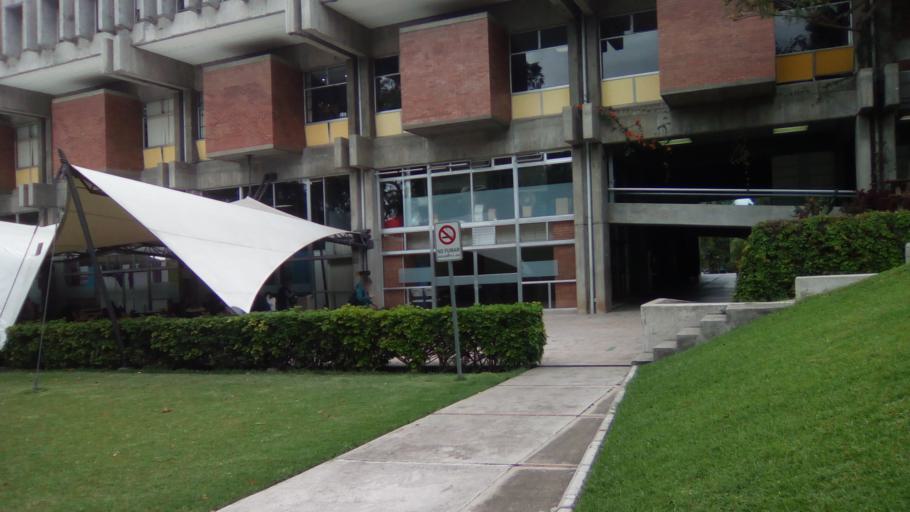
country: GT
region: Guatemala
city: Santa Catarina Pinula
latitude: 14.5946
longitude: -90.4846
